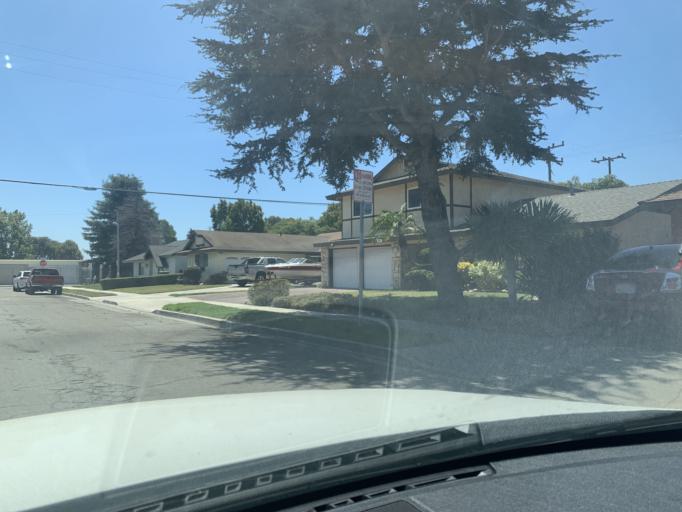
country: US
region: California
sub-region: Ventura County
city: Oxnard
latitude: 34.2152
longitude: -119.1913
